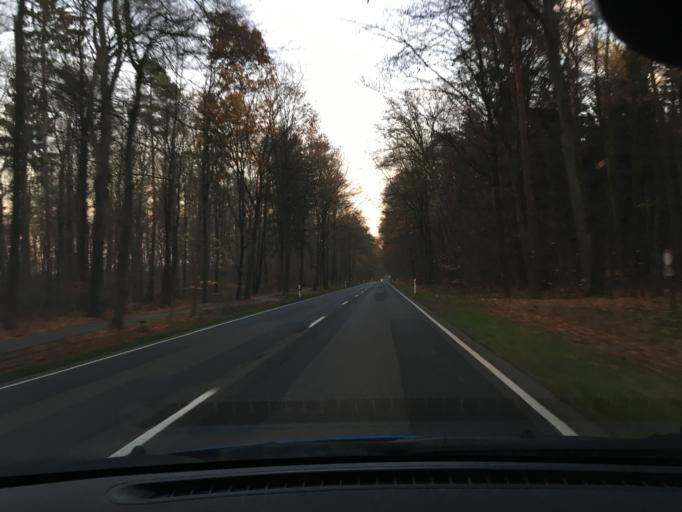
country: DE
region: Lower Saxony
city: Uelzen
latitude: 52.9803
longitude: 10.5305
